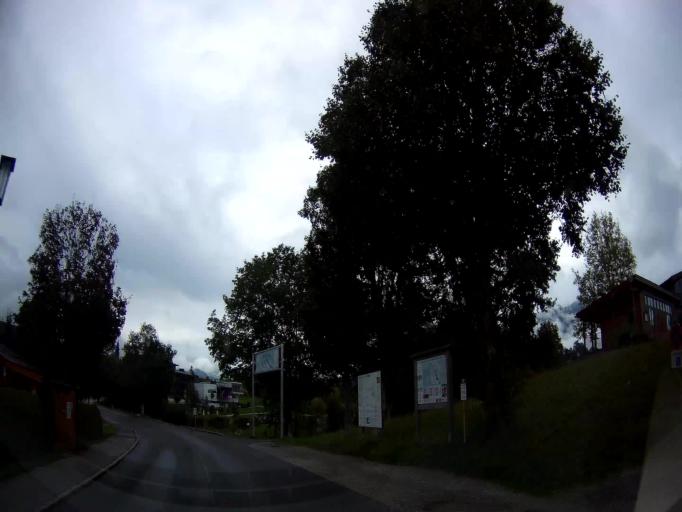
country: AT
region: Salzburg
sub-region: Politischer Bezirk Zell am See
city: Saalfelden am Steinernen Meer
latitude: 47.4208
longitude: 12.8449
